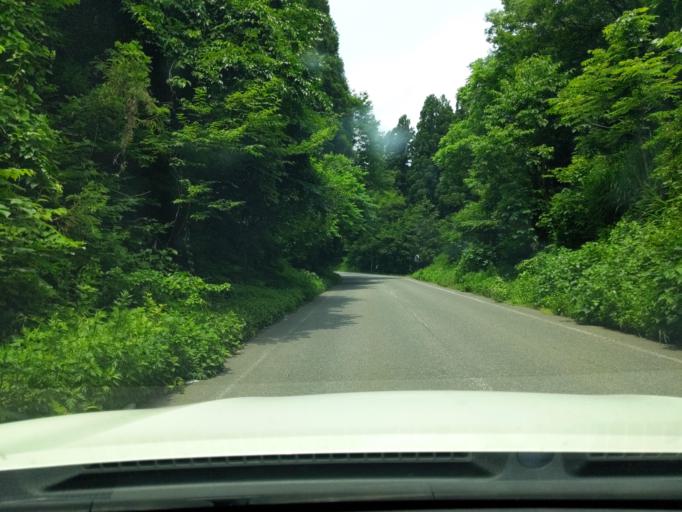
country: JP
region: Niigata
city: Kashiwazaki
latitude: 37.3369
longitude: 138.5556
